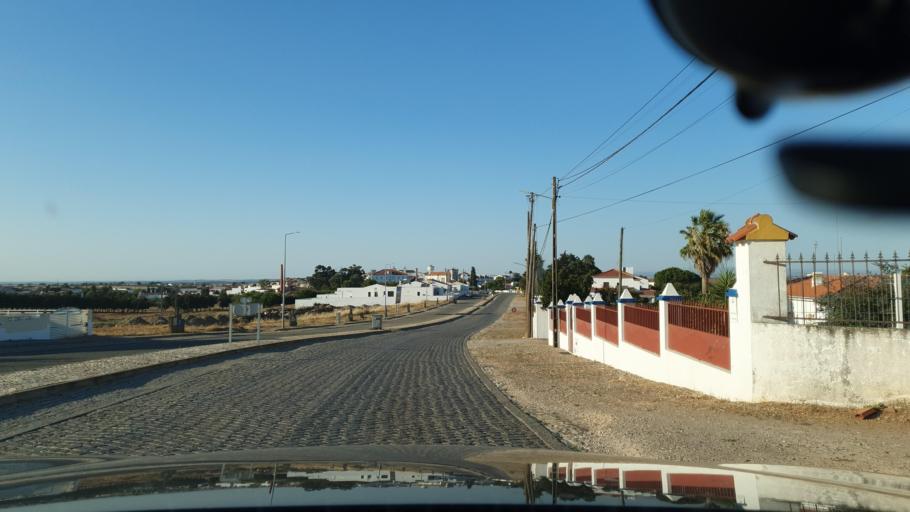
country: PT
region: Portalegre
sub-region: Fronteira
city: Fronteira
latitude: 38.9450
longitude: -7.6771
